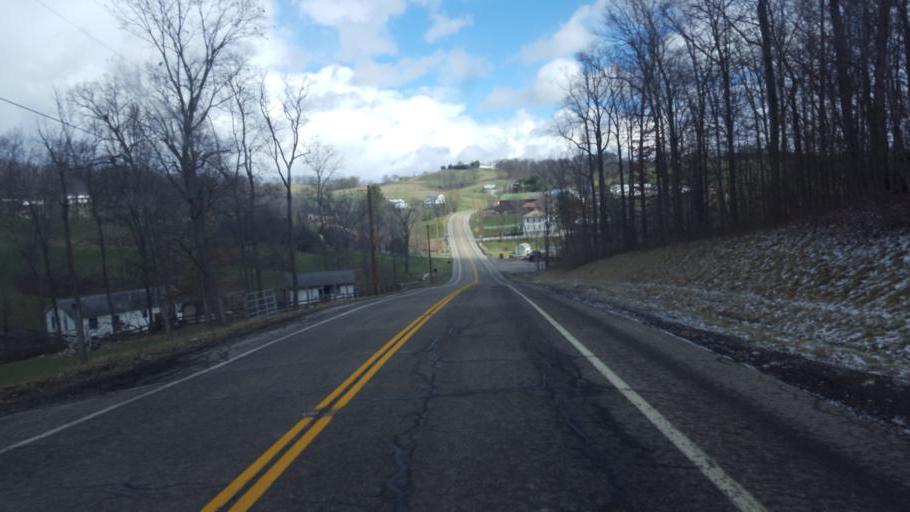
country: US
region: Ohio
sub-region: Tuscarawas County
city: Sugarcreek
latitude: 40.4411
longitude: -81.7399
